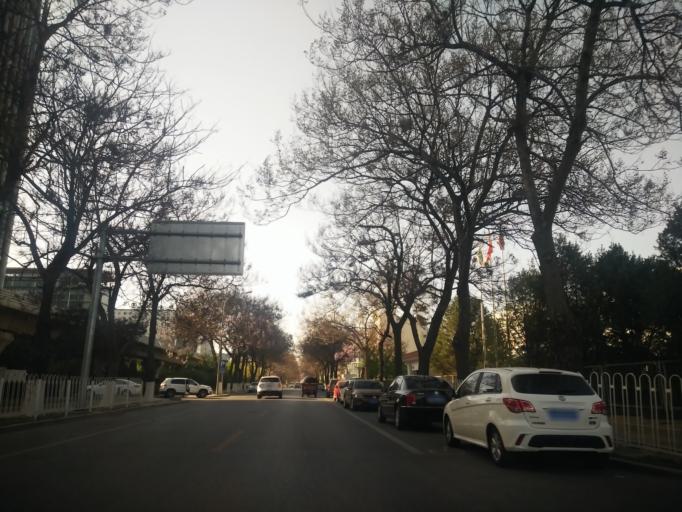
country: CN
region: Beijing
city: Jiugong
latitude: 39.7950
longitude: 116.5054
